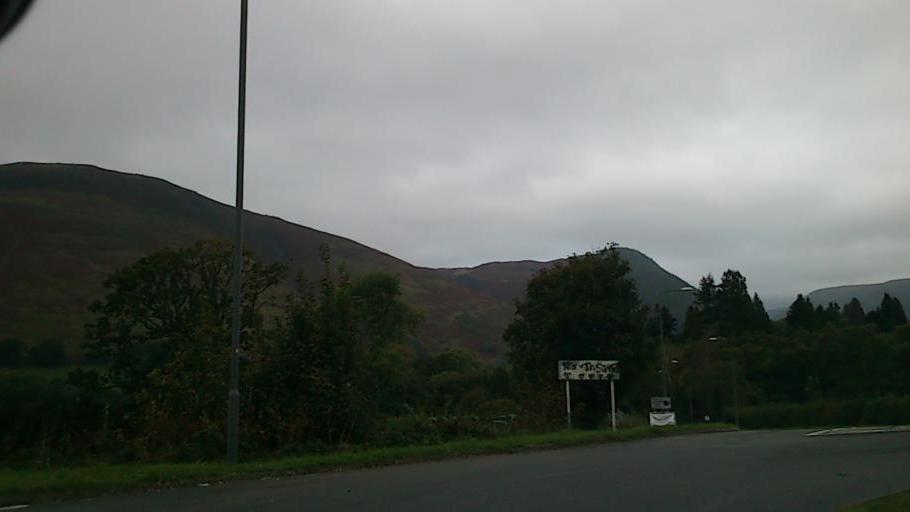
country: GB
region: Wales
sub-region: Gwynedd
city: Corris
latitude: 52.6984
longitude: -3.6848
